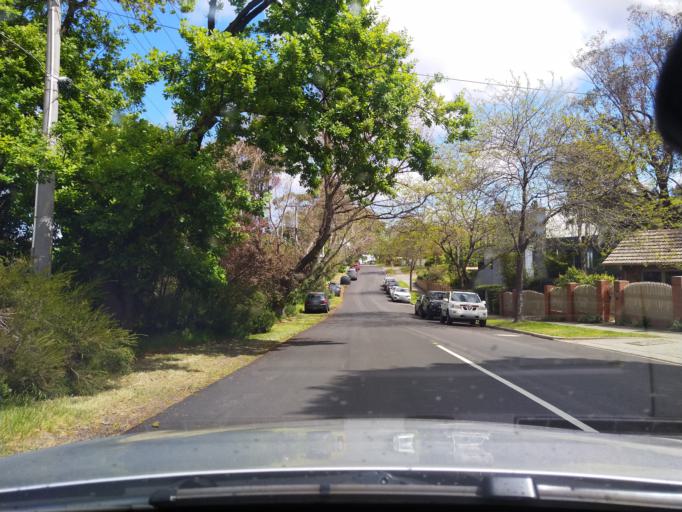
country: AU
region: Victoria
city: Ivanhoe East
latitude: -37.7660
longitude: 145.0502
